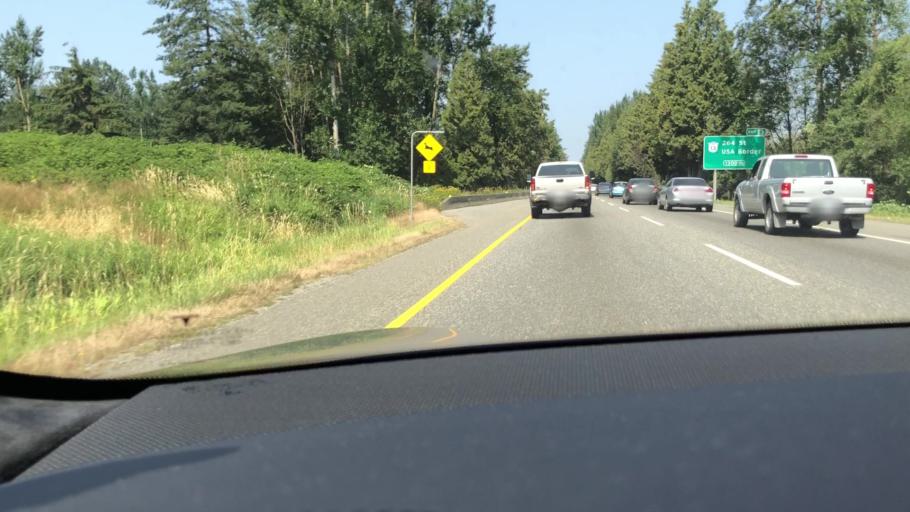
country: CA
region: British Columbia
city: Aldergrove
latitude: 49.0941
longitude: -122.4733
